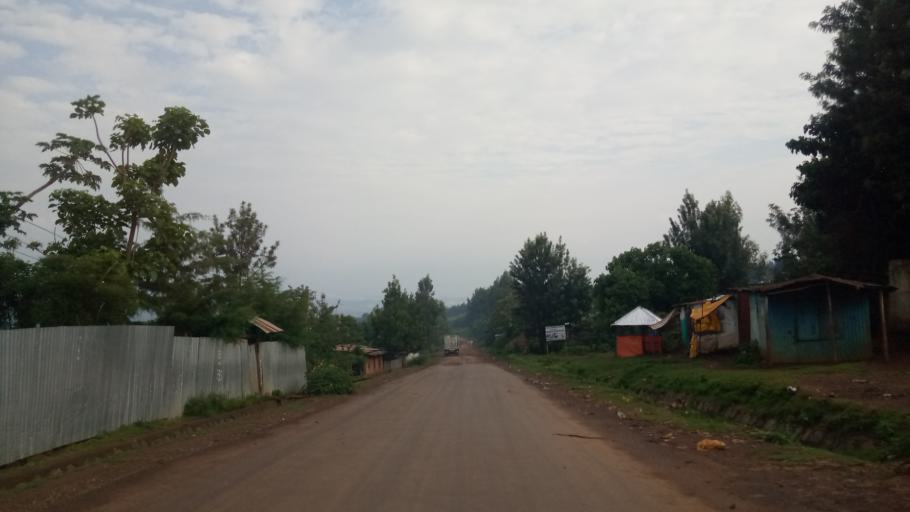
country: ET
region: Oromiya
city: Agaro
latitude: 7.7908
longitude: 36.7265
